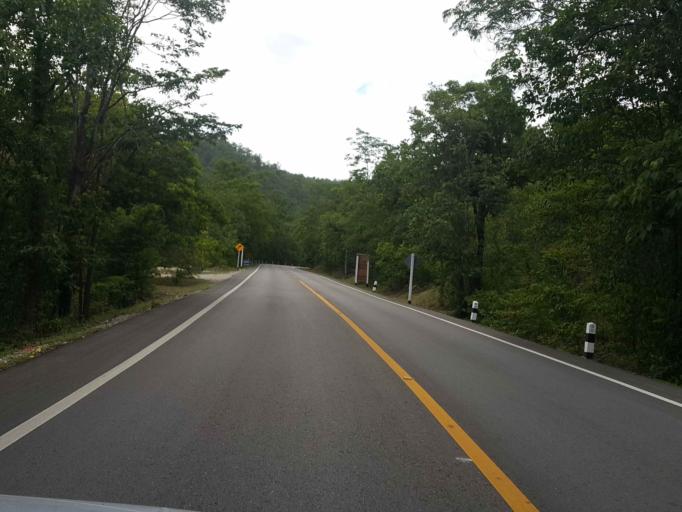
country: TH
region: Chiang Mai
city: Chom Thong
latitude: 18.5049
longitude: 98.6652
